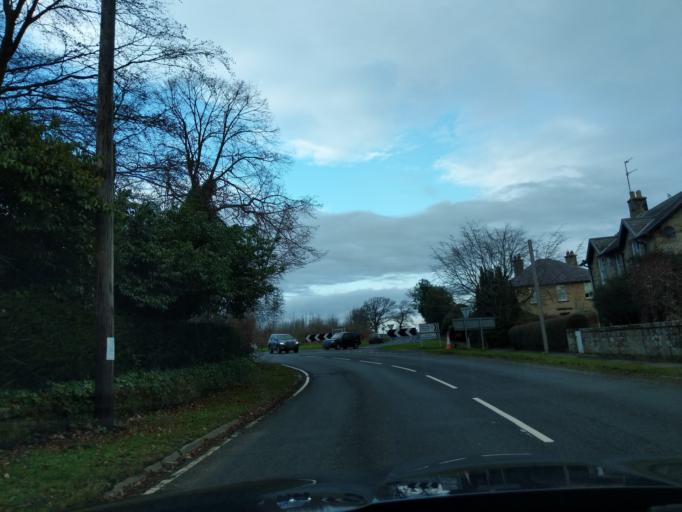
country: GB
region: England
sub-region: Northumberland
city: Meldon
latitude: 55.1053
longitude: -1.8437
